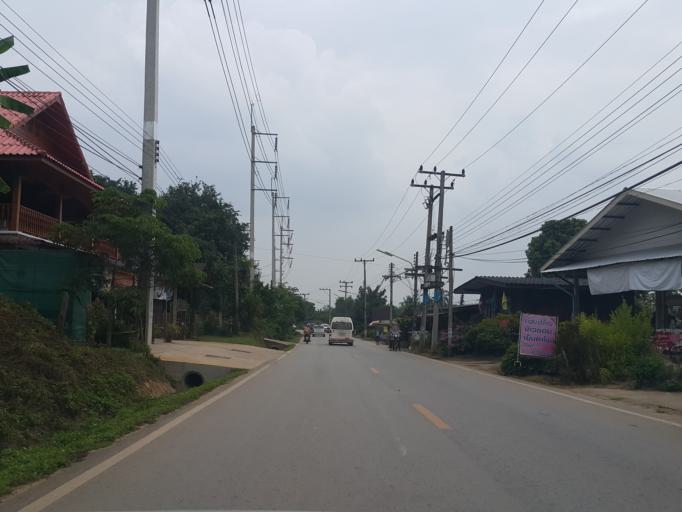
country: TH
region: Chiang Mai
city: Mae Taeng
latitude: 19.1014
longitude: 98.8410
